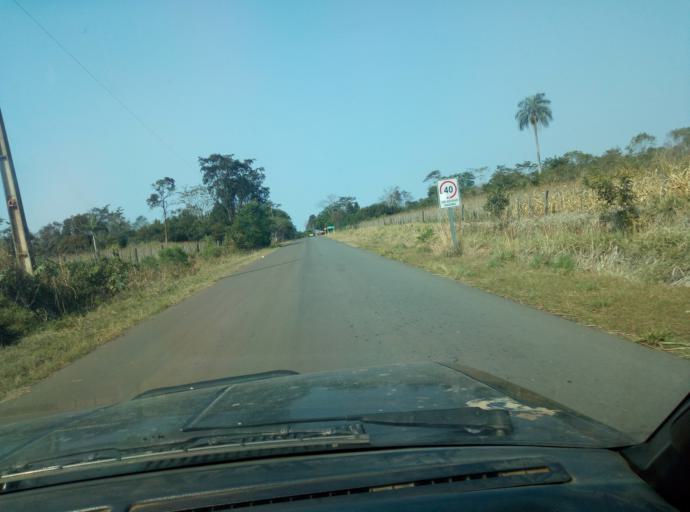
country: PY
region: Caaguazu
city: Carayao
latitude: -25.2076
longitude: -56.3064
